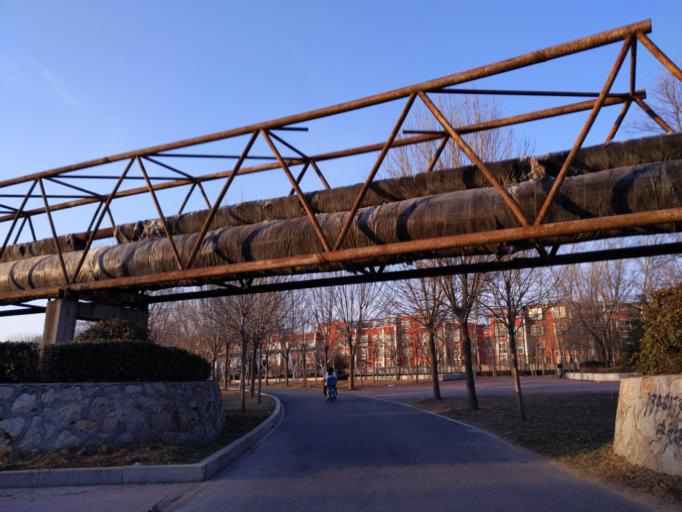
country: CN
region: Henan Sheng
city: Puyang
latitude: 35.7695
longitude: 114.9982
